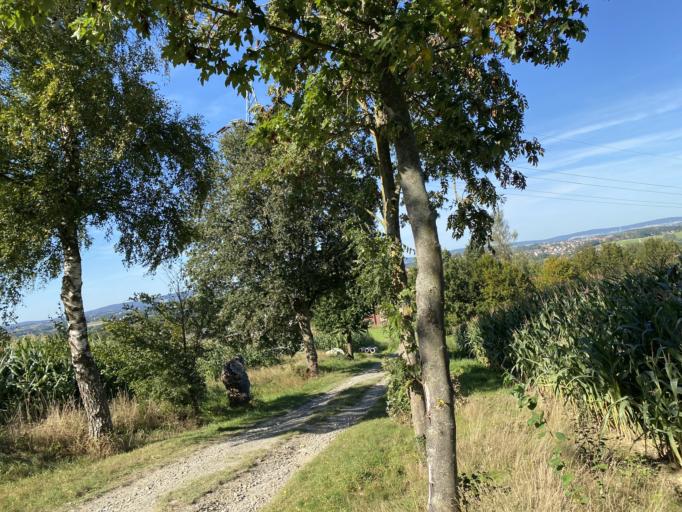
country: DE
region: North Rhine-Westphalia
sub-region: Regierungsbezirk Detmold
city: Kirchlengern
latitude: 52.1816
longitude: 8.6396
